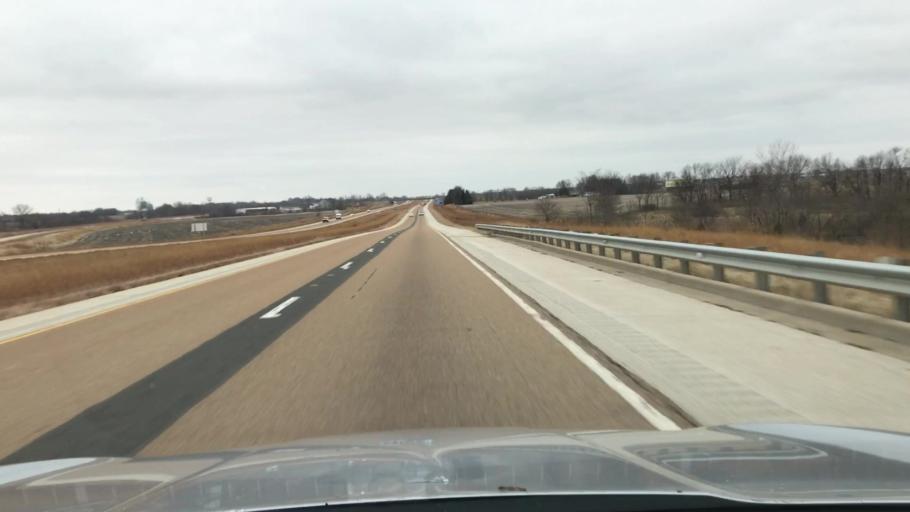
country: US
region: Illinois
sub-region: Montgomery County
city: Litchfield
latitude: 39.2139
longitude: -89.6530
